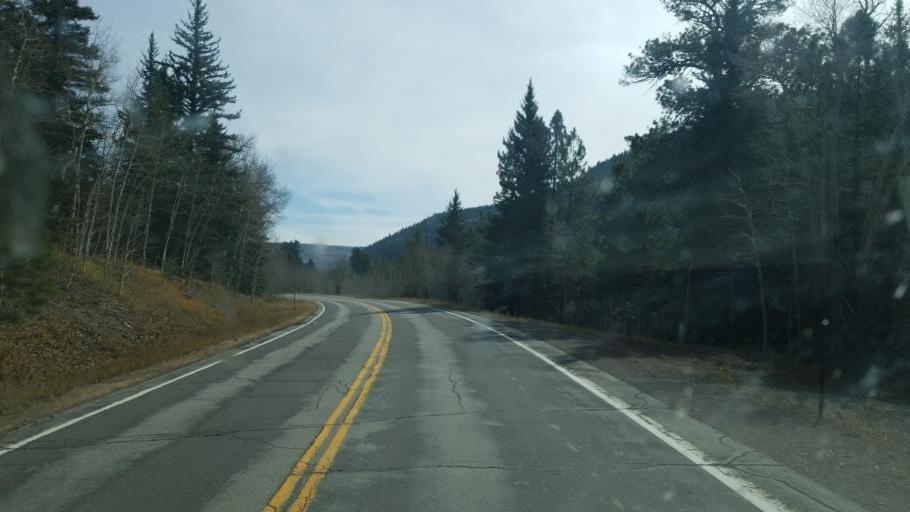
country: US
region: Colorado
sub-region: Conejos County
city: Conejos
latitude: 37.1141
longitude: -106.3218
